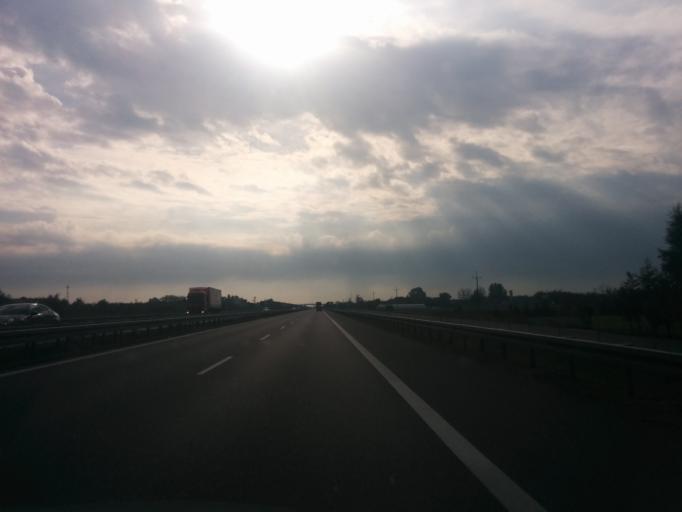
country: PL
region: Masovian Voivodeship
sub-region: Powiat bialobrzeski
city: Stara Blotnica
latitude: 51.5541
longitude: 21.0364
